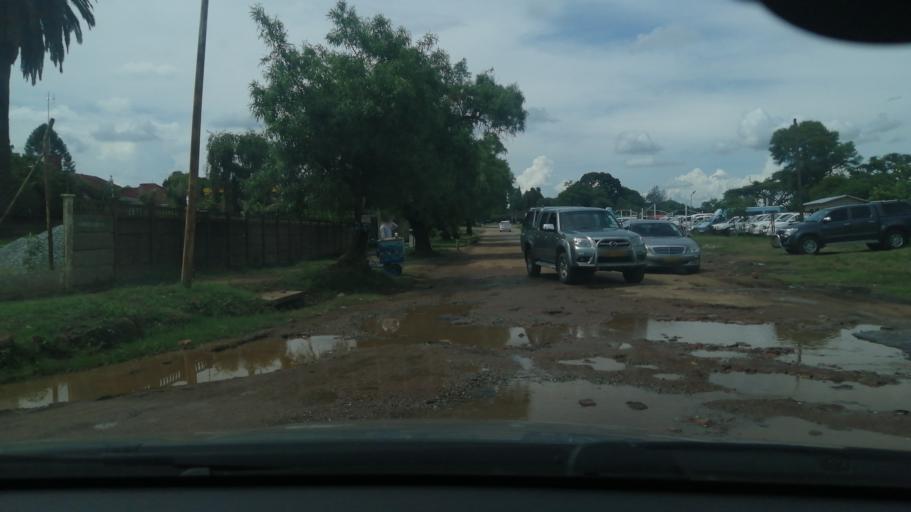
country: ZW
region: Harare
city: Harare
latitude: -17.8199
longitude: 31.0707
